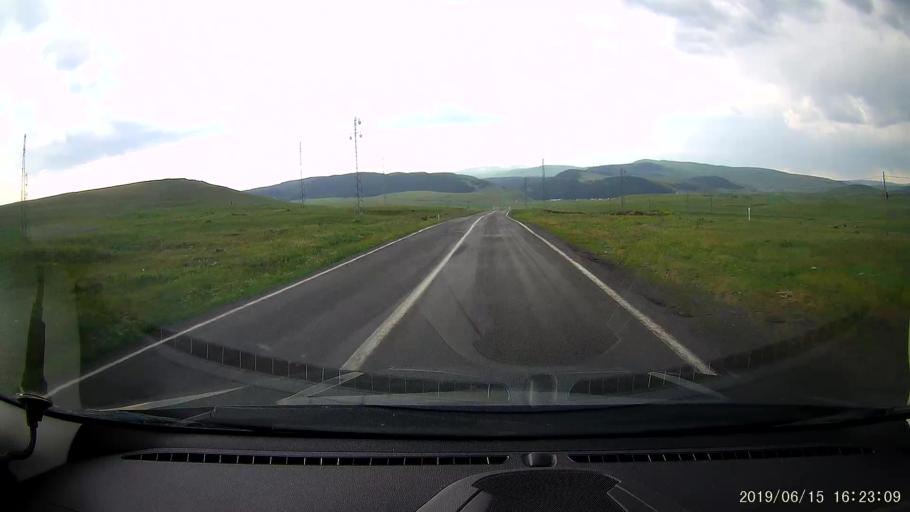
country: TR
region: Ardahan
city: Hanak
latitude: 41.1806
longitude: 42.8590
